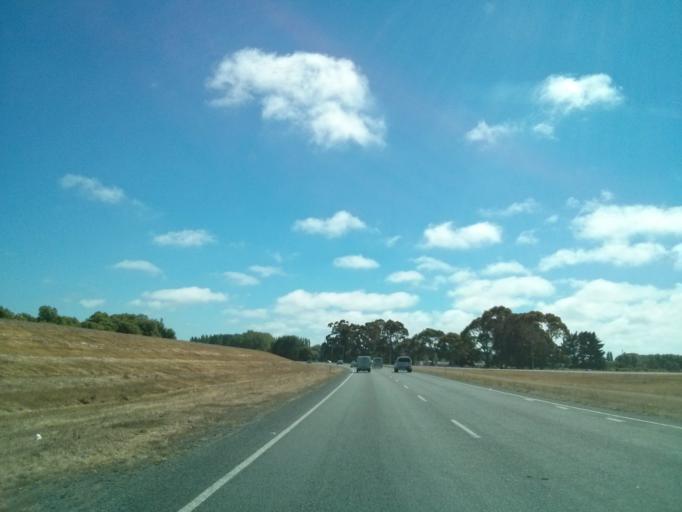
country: NZ
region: Canterbury
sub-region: Waimakariri District
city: Kaiapoi
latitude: -43.4253
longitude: 172.6478
